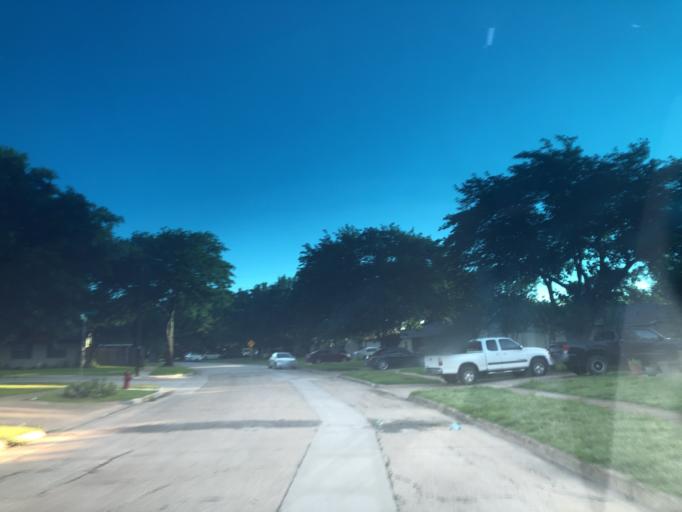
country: US
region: Texas
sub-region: Dallas County
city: Grand Prairie
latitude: 32.7041
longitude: -97.0116
